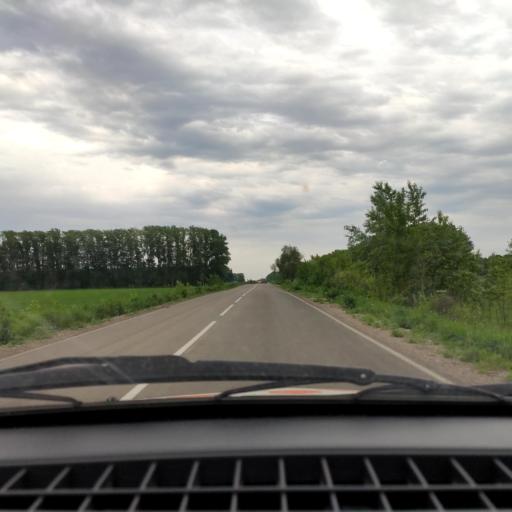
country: RU
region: Bashkortostan
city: Avdon
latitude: 54.5357
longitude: 55.7635
